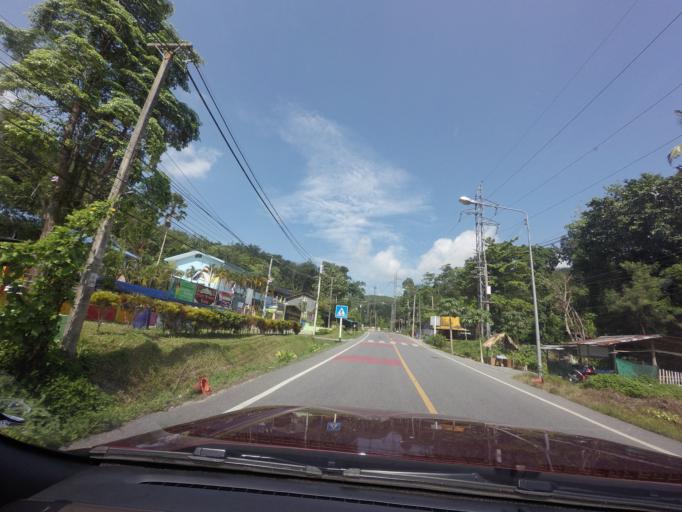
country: TH
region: Yala
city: Betong
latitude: 5.8712
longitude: 101.1302
